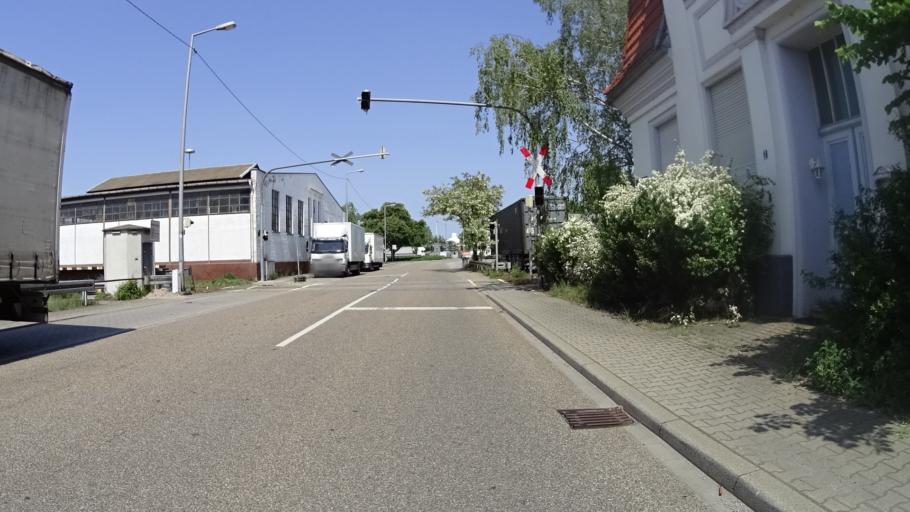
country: DE
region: Rheinland-Pfalz
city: Altrip
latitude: 49.4198
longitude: 8.5148
